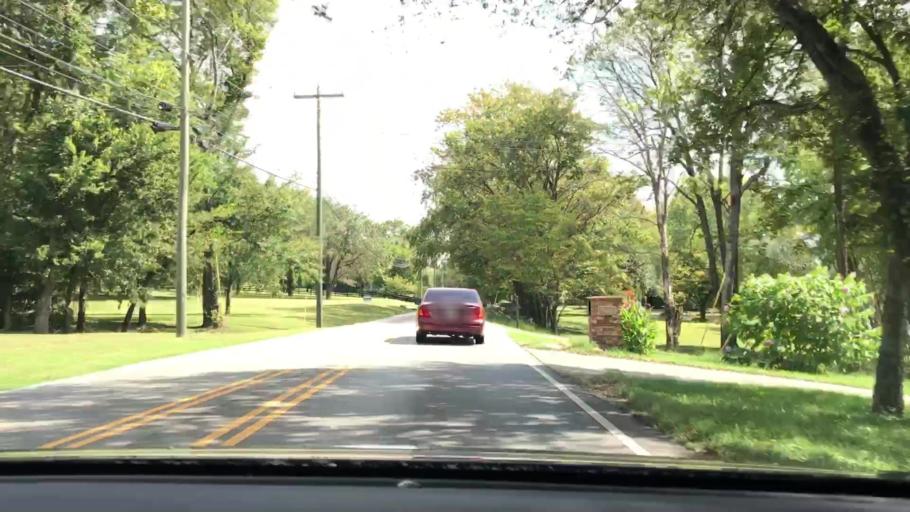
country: US
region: Tennessee
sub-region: Williamson County
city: Brentwood Estates
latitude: 36.0150
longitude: -86.7353
